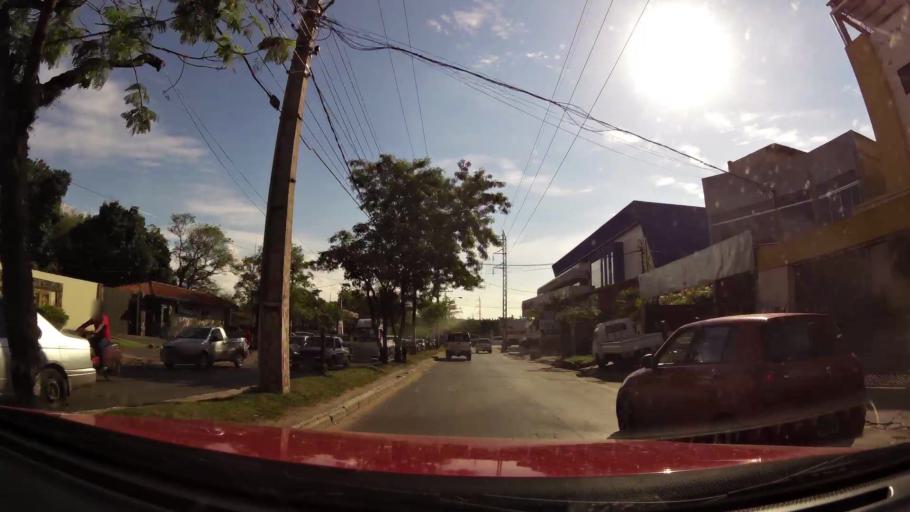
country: PY
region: Asuncion
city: Asuncion
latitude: -25.2558
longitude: -57.5832
